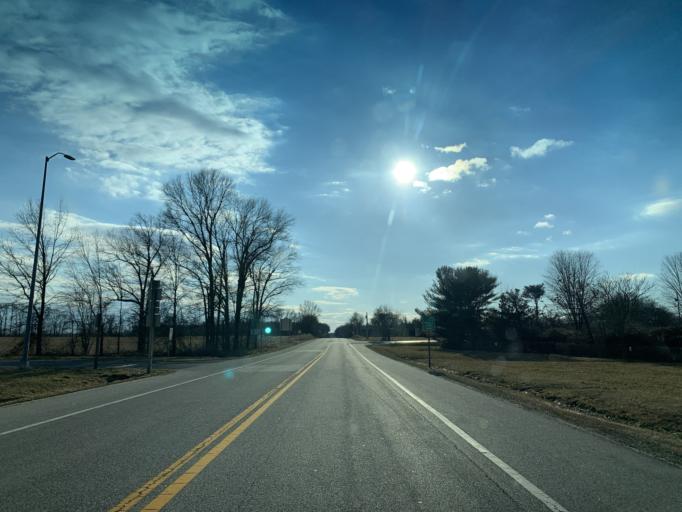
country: US
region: Maryland
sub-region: Queen Anne's County
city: Kingstown
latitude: 39.1727
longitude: -75.9187
